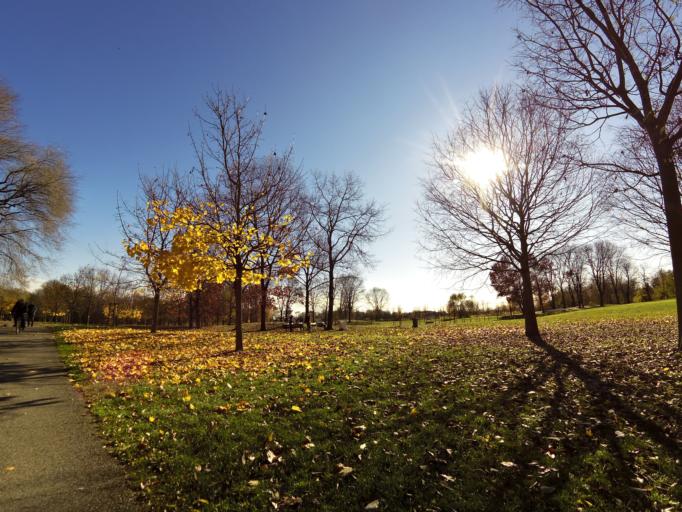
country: IT
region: Lombardy
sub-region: Citta metropolitana di Milano
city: Chiaravalle
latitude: 45.4334
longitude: 9.2333
